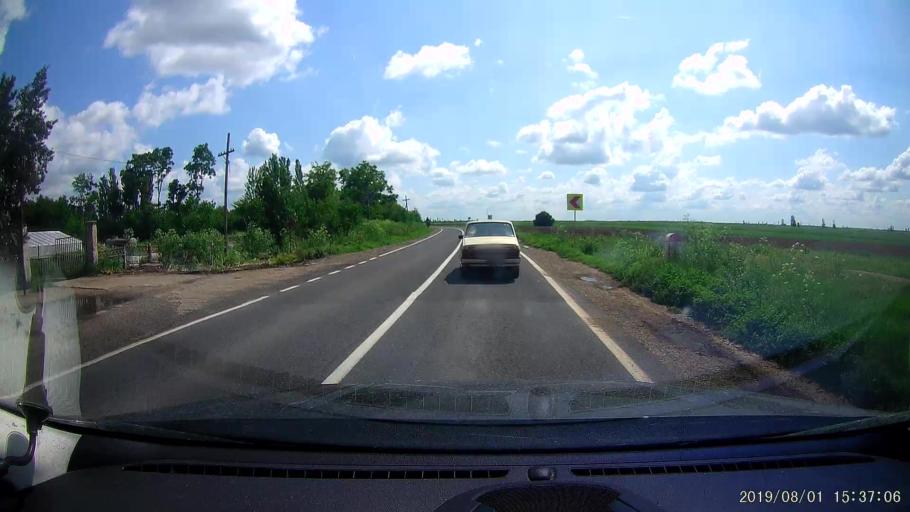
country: RO
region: Braila
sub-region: Comuna Insuratei
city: Insuratei
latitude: 44.9052
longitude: 27.5909
